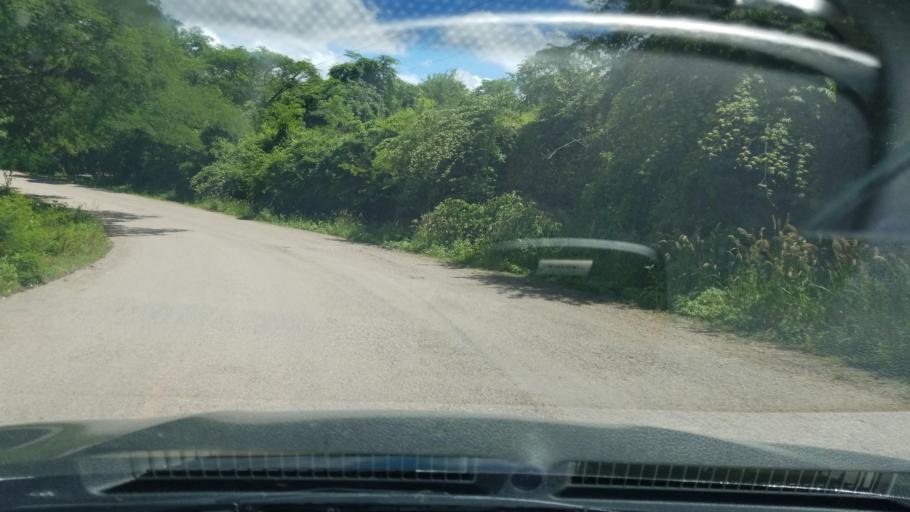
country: HN
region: Francisco Morazan
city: San Juan de Flores
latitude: 14.3149
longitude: -87.0393
